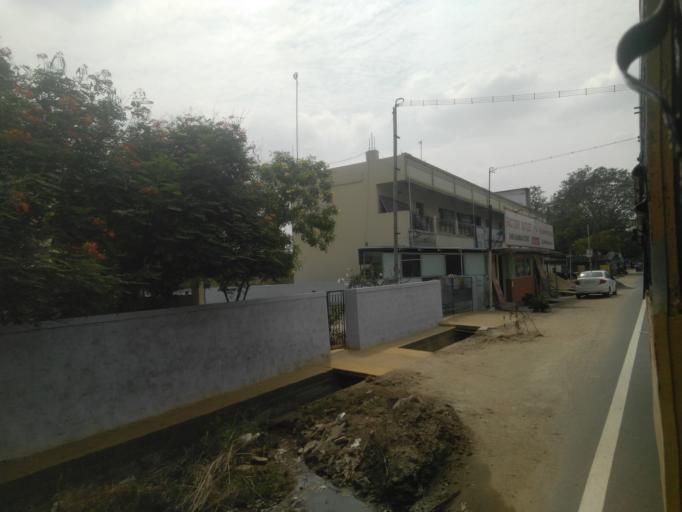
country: IN
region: Tamil Nadu
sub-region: Coimbatore
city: Irugur
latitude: 11.0081
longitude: 77.0749
